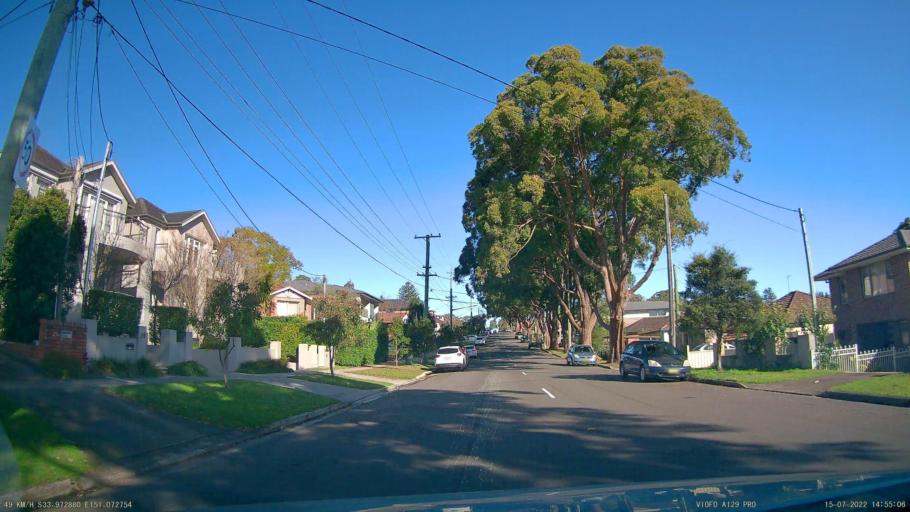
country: AU
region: New South Wales
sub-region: Hurstville
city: Oatley
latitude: -33.9730
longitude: 151.0727
